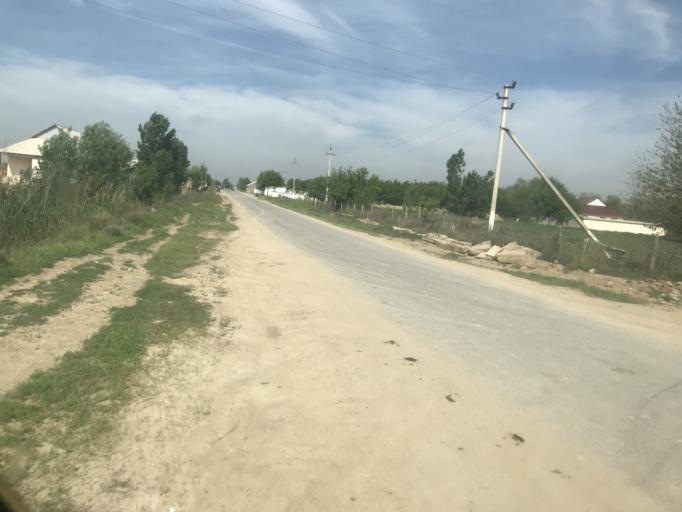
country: UZ
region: Jizzax
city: Gagarin
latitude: 40.9038
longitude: 68.0934
